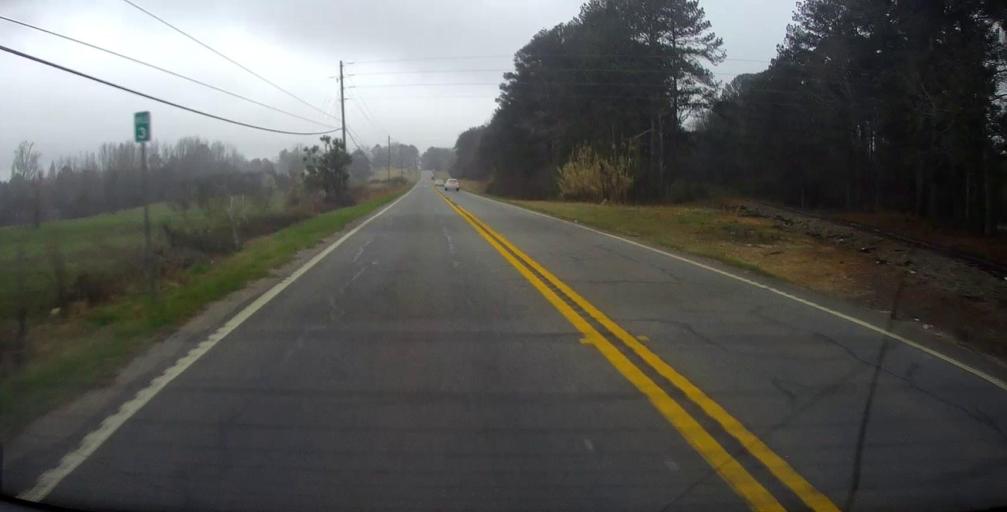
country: US
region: Georgia
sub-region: Spalding County
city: Experiment
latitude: 33.2185
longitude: -84.3146
